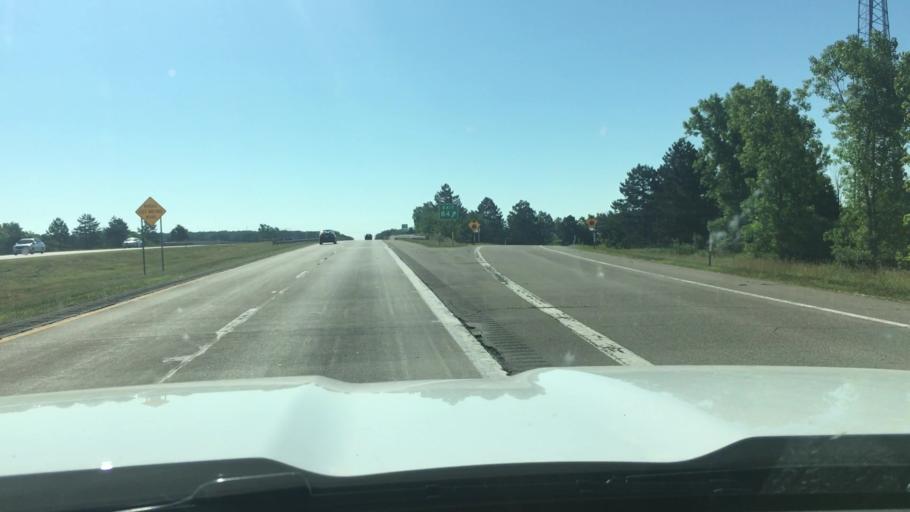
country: US
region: Michigan
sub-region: Eaton County
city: Grand Ledge
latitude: 42.8138
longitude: -84.7912
